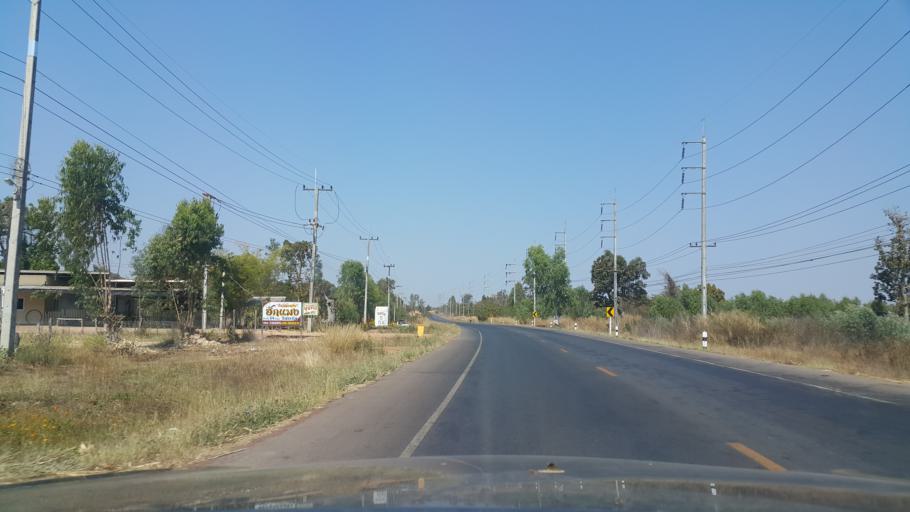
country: TH
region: Changwat Udon Thani
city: Thung Fon
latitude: 17.4147
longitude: 103.1851
